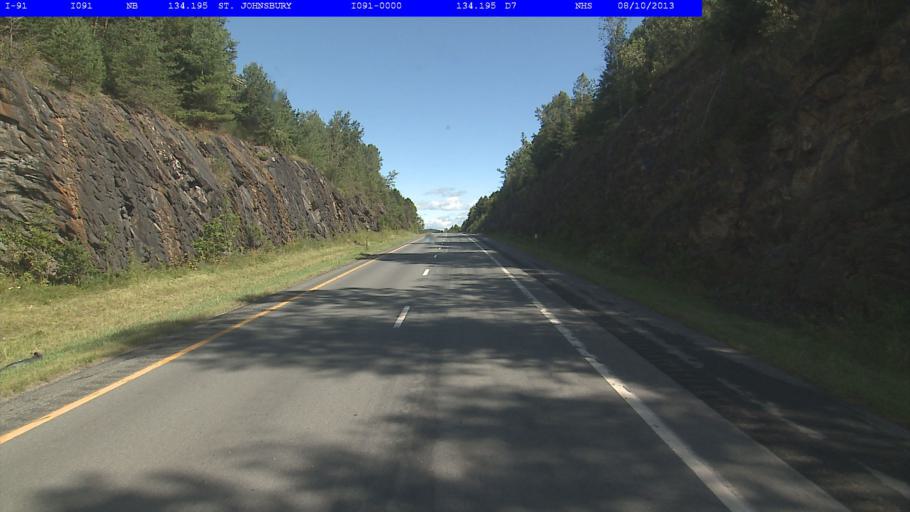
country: US
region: Vermont
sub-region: Caledonia County
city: Lyndon
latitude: 44.4772
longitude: -72.0234
